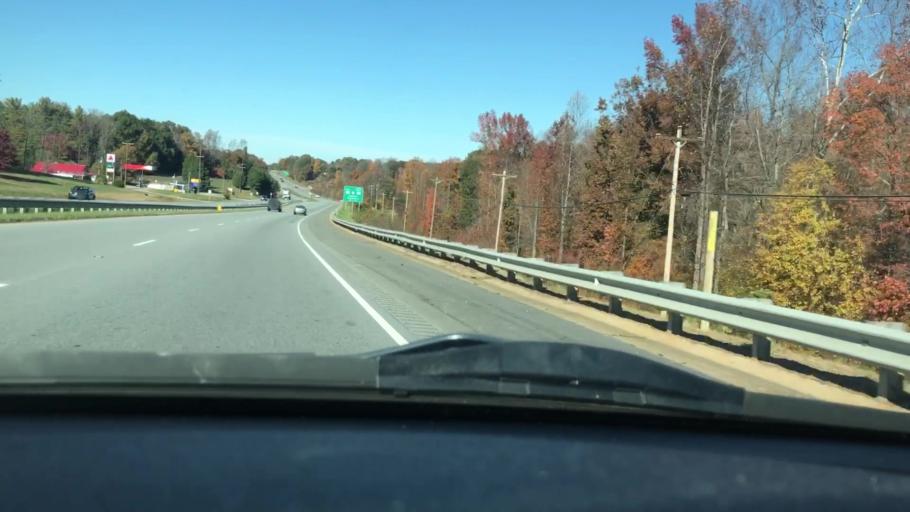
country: US
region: North Carolina
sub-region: Rockingham County
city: Madison
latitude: 36.3572
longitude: -79.9465
